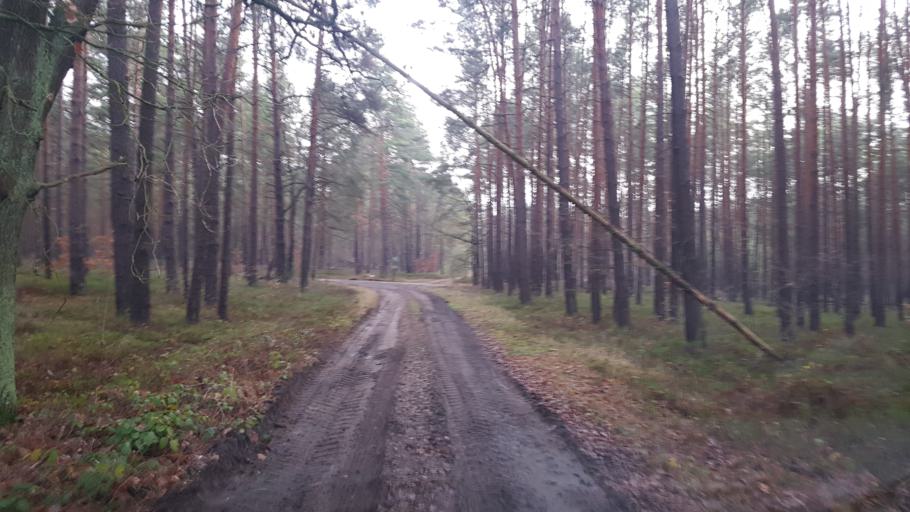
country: DE
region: Brandenburg
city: Ruckersdorf
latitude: 51.5852
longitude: 13.6209
